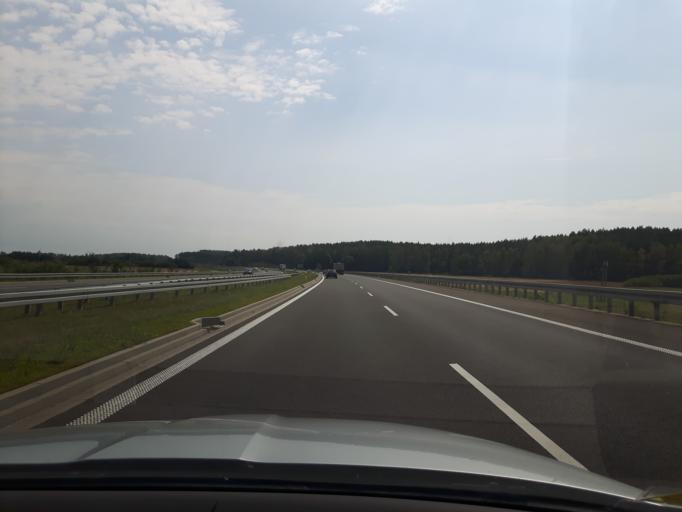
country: PL
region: Warmian-Masurian Voivodeship
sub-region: Powiat nidzicki
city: Nidzica
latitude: 53.3812
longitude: 20.3731
